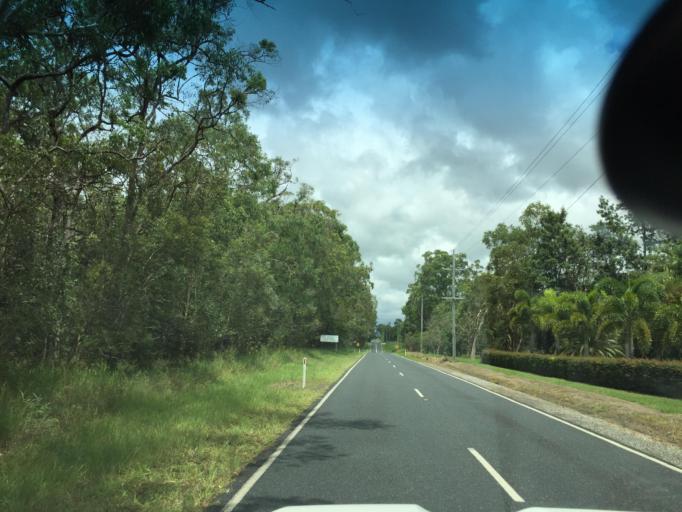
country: AU
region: Queensland
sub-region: Moreton Bay
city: Caboolture
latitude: -27.0482
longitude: 152.9122
